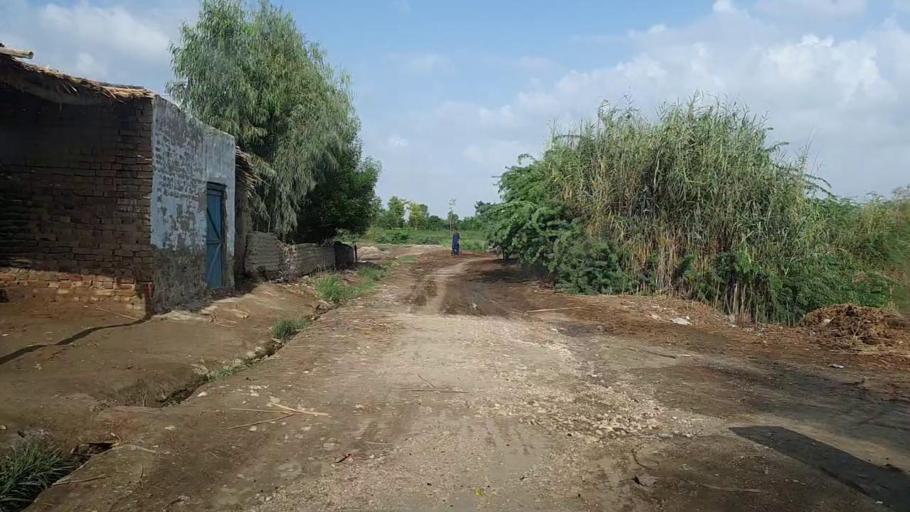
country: PK
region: Sindh
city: Bhiria
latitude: 26.8386
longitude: 68.2399
